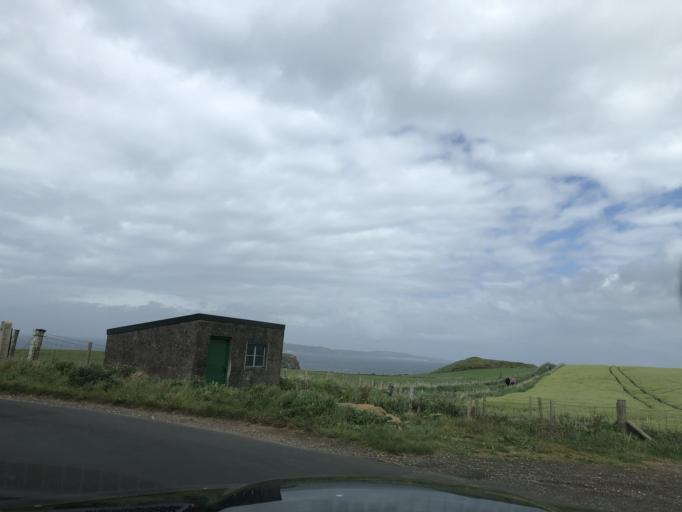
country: GB
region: Northern Ireland
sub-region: Moyle District
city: Ballycastle
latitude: 55.2401
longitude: -6.3661
